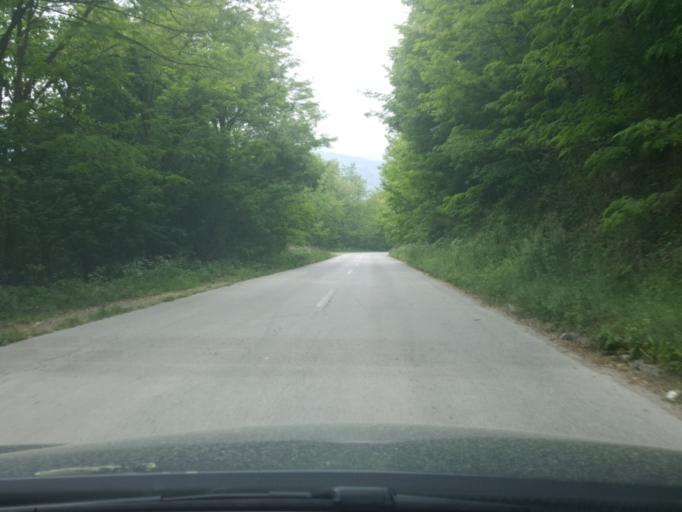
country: RS
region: Central Serbia
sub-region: Zlatiborski Okrug
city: Bajina Basta
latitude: 43.9583
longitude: 19.5509
